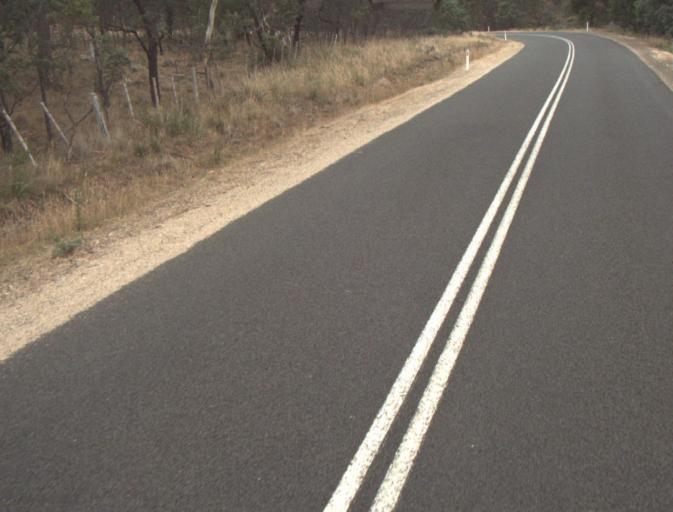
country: AU
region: Tasmania
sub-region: Northern Midlands
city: Evandale
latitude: -41.5131
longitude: 147.3333
